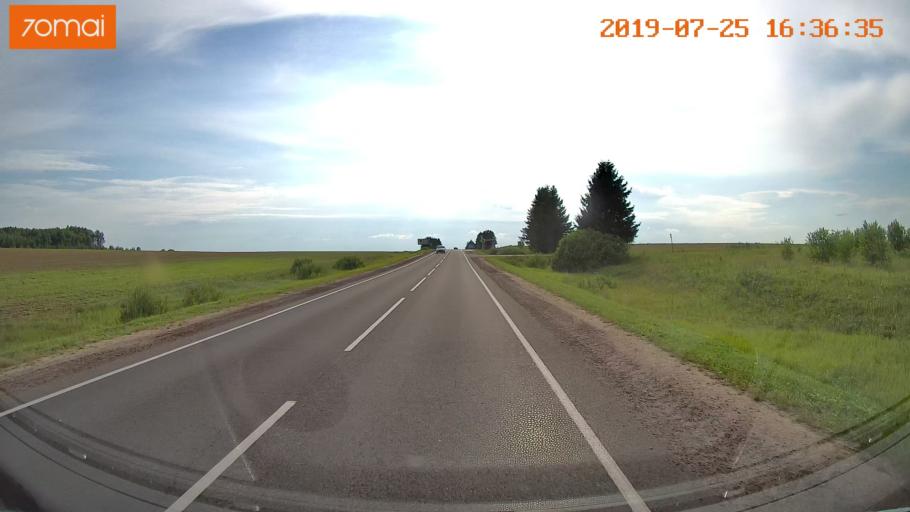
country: RU
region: Ivanovo
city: Privolzhsk
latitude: 57.3953
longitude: 41.3979
